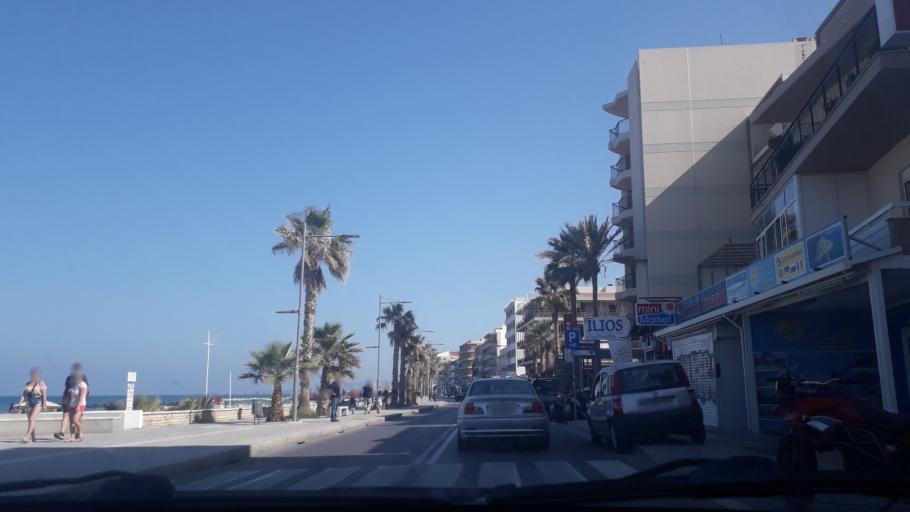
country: GR
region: Crete
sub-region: Nomos Rethymnis
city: Rethymno
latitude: 35.3665
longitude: 24.4859
